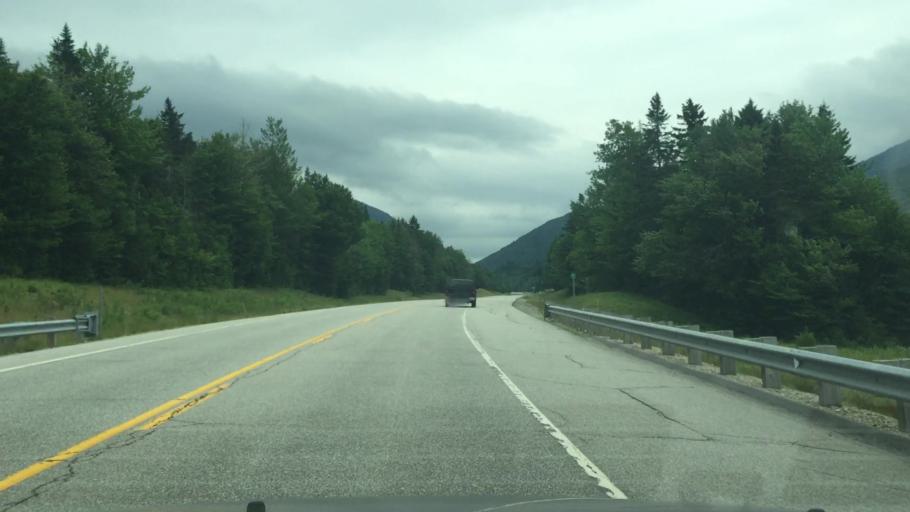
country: US
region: New Hampshire
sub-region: Coos County
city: Jefferson
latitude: 44.2367
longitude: -71.4232
